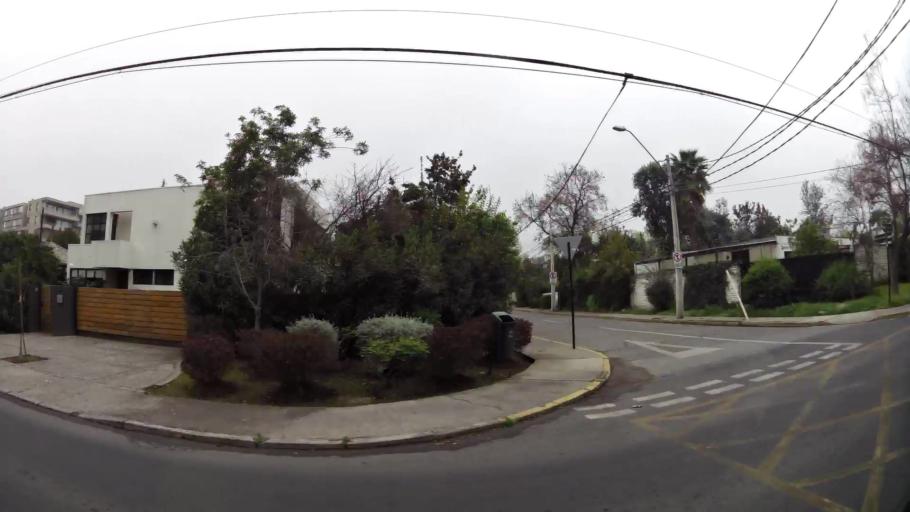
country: CL
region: Santiago Metropolitan
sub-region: Provincia de Santiago
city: Villa Presidente Frei, Nunoa, Santiago, Chile
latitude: -33.4016
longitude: -70.5846
